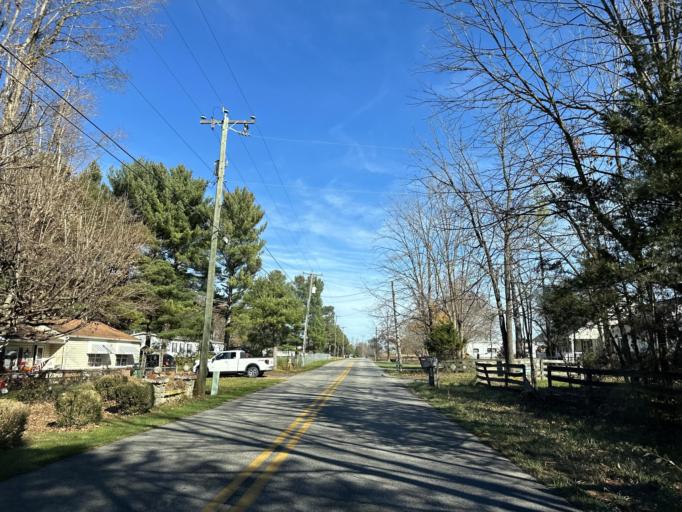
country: US
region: Virginia
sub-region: Augusta County
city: Crimora
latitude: 38.2090
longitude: -78.9024
